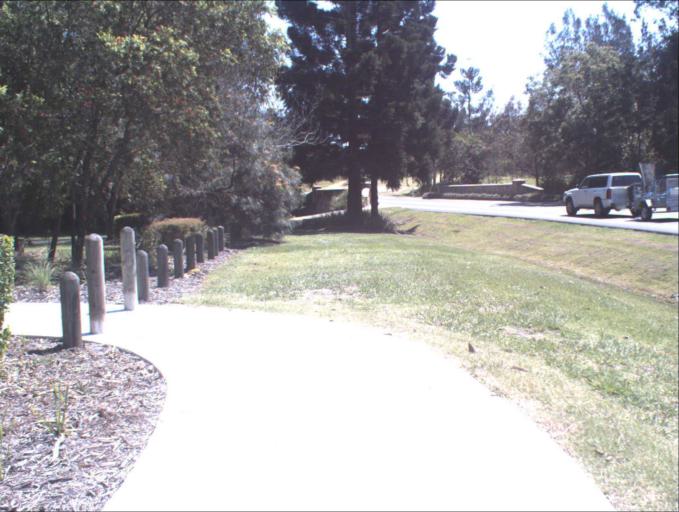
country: AU
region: Queensland
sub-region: Logan
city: North Maclean
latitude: -27.8153
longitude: 152.9663
